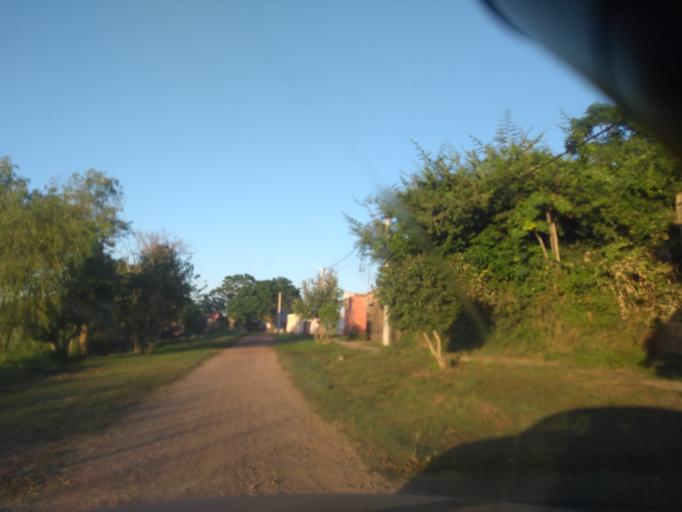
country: AR
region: Chaco
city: Resistencia
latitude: -27.4564
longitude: -58.9673
